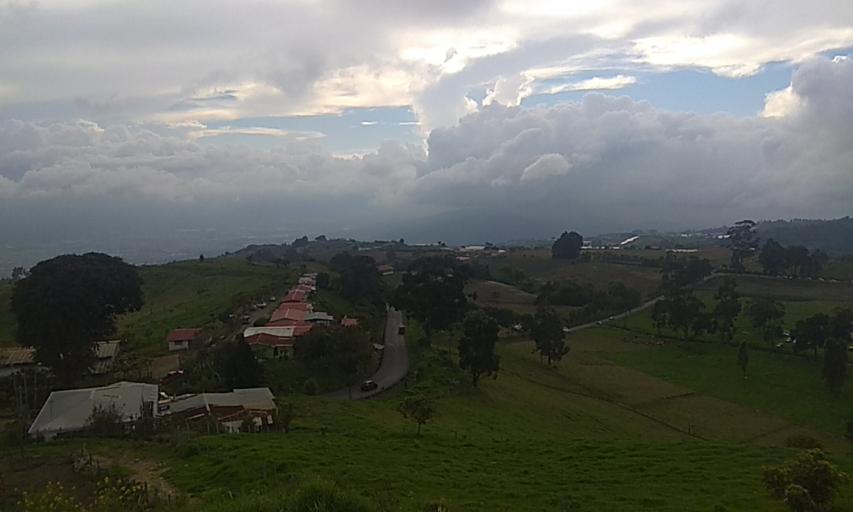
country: CR
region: Cartago
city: Cot
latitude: 9.9318
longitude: -83.8794
